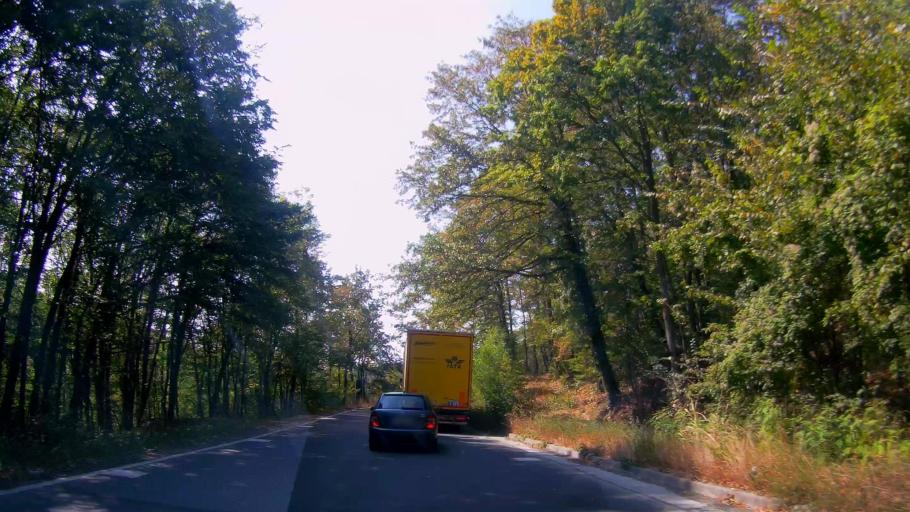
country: BG
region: Shumen
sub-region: Obshtina Smyadovo
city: Smyadovo
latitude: 42.9328
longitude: 26.9505
